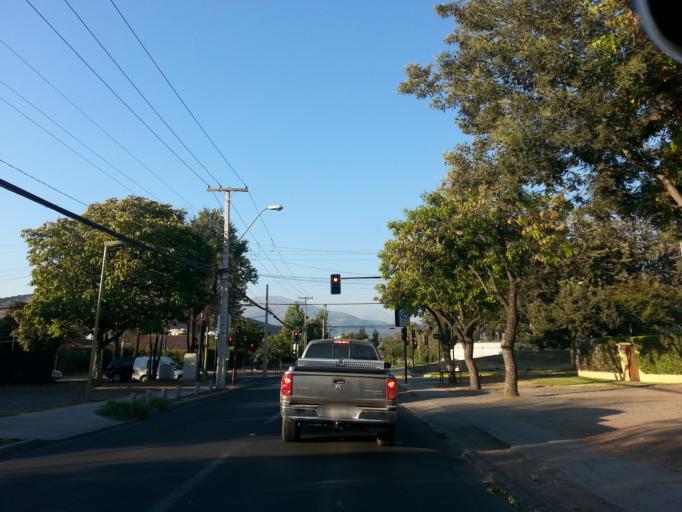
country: CL
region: Santiago Metropolitan
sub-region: Provincia de Santiago
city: Villa Presidente Frei, Nunoa, Santiago, Chile
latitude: -33.3927
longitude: -70.5385
